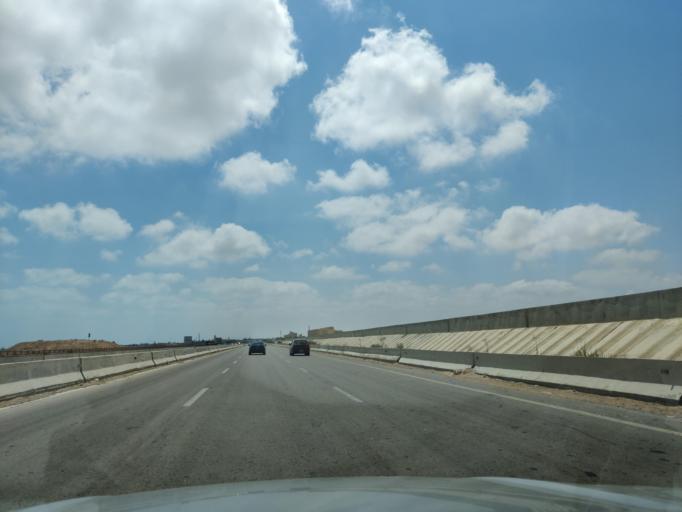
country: EG
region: Muhafazat Matruh
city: Al `Alamayn
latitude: 30.8215
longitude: 29.0062
